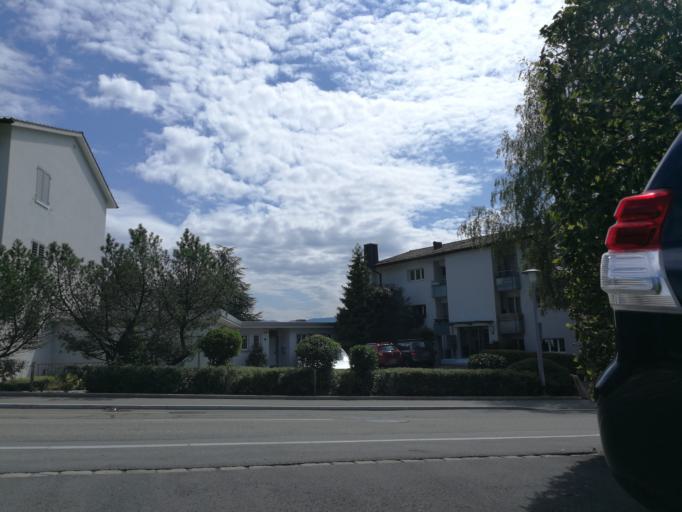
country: CH
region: Zurich
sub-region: Bezirk Meilen
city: Feldmeilen
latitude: 47.2824
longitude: 8.6146
